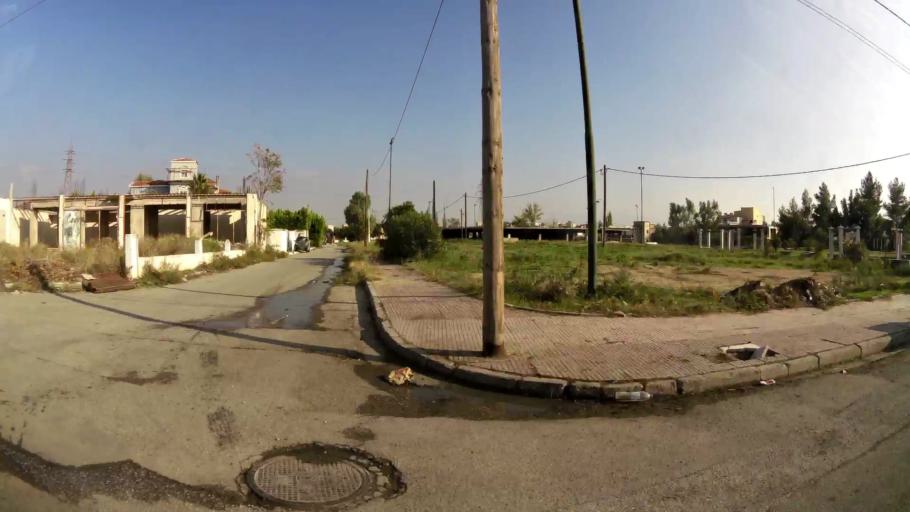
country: GR
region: Attica
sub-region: Nomarchia Dytikis Attikis
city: Zefyri
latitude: 38.0764
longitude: 23.7216
